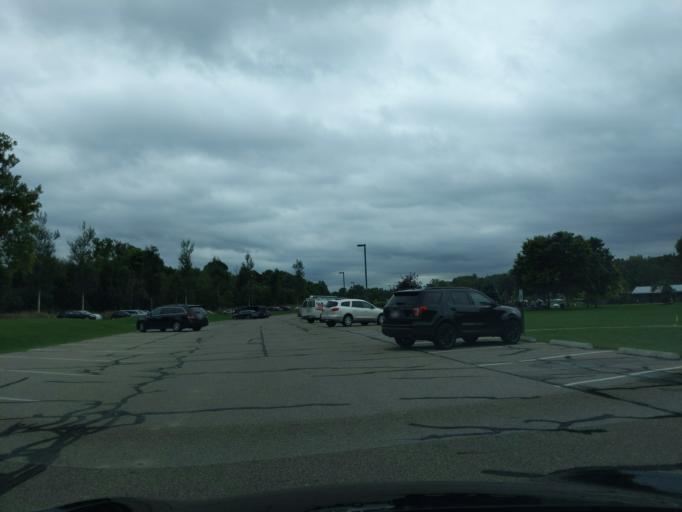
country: US
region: Michigan
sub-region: Ingham County
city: Lansing
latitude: 42.6957
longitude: -84.5293
